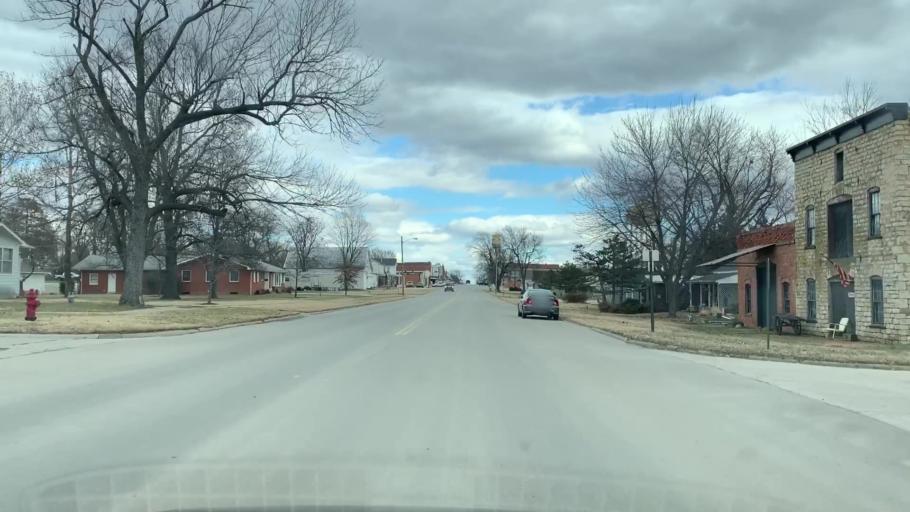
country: US
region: Kansas
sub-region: Allen County
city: Humboldt
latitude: 37.8112
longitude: -95.4421
